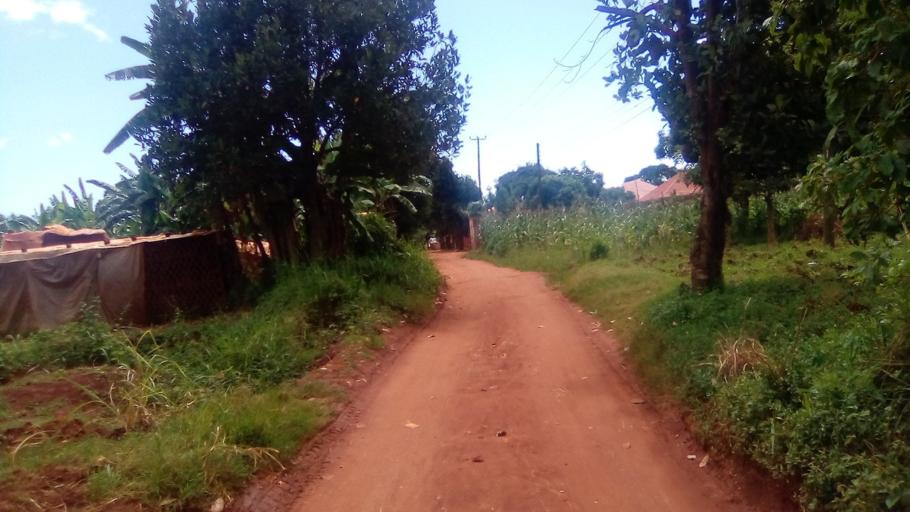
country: UG
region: Central Region
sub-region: Wakiso District
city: Entebbe
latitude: 0.1016
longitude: 32.5276
